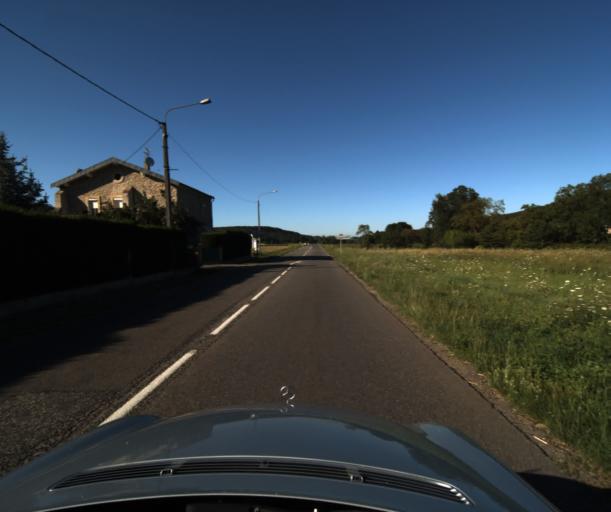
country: FR
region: Midi-Pyrenees
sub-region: Departement de l'Ariege
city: Lavelanet
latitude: 42.9975
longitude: 1.8798
